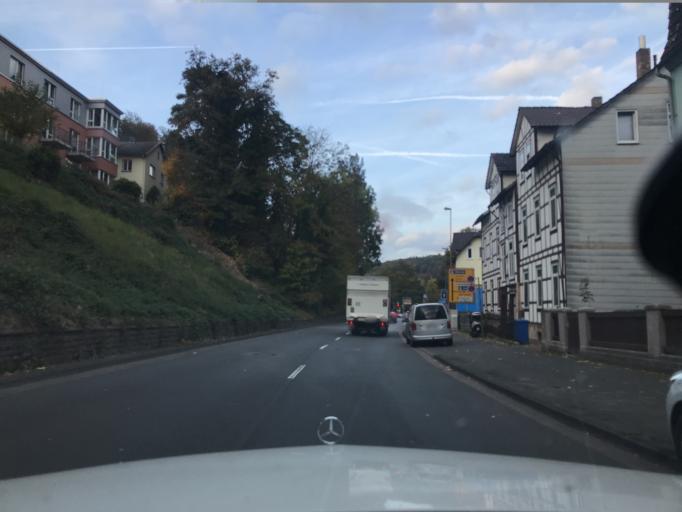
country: DE
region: Lower Saxony
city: Hannoversch Munden
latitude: 51.4137
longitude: 9.6444
